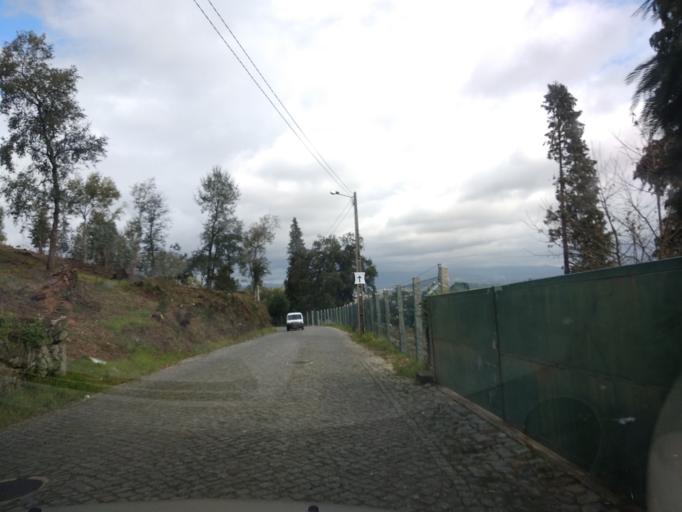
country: PT
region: Braga
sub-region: Braga
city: Braga
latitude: 41.5449
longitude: -8.4434
